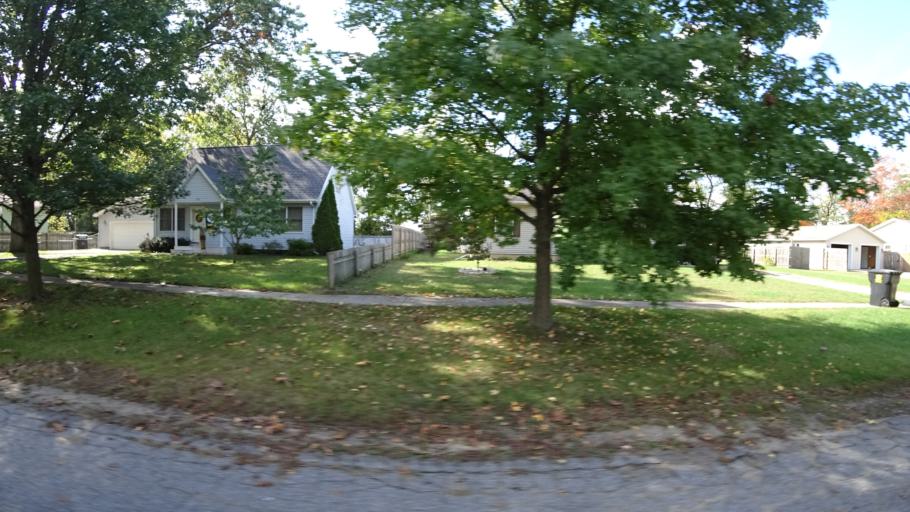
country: US
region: Michigan
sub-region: Saint Joseph County
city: Three Rivers
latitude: 41.9531
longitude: -85.6147
